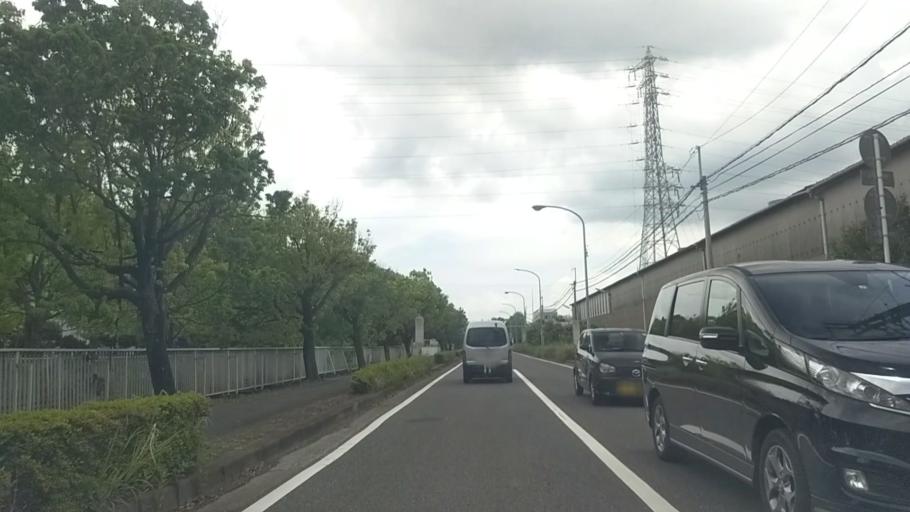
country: JP
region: Kanagawa
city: Fujisawa
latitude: 35.3718
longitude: 139.5226
